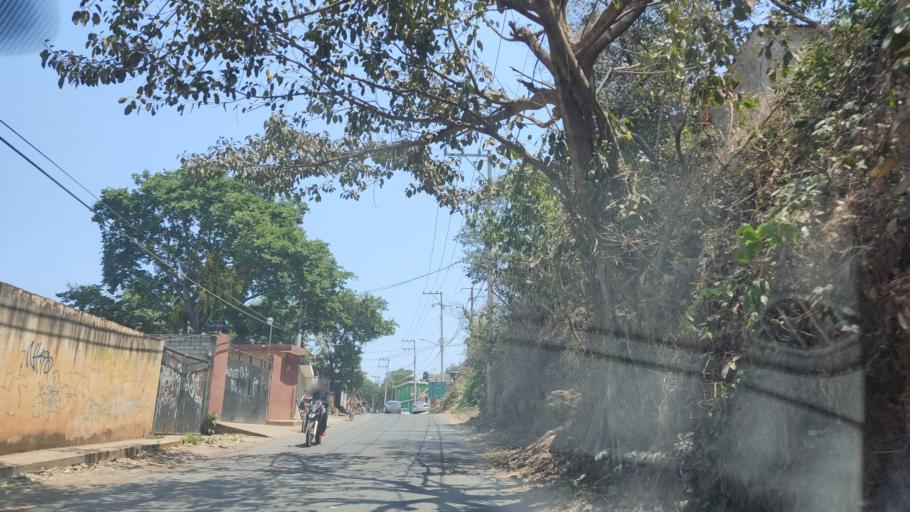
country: MX
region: Nayarit
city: Puga
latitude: 21.5851
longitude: -104.8162
